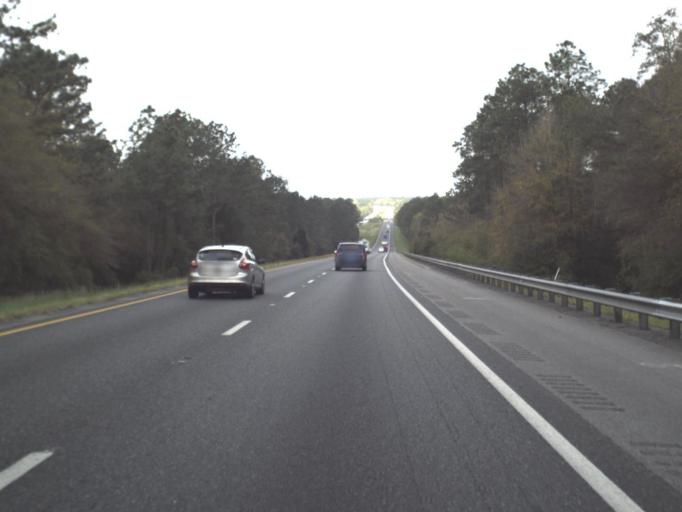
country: US
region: Florida
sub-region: Okaloosa County
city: Crestview
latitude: 30.7147
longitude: -86.6304
